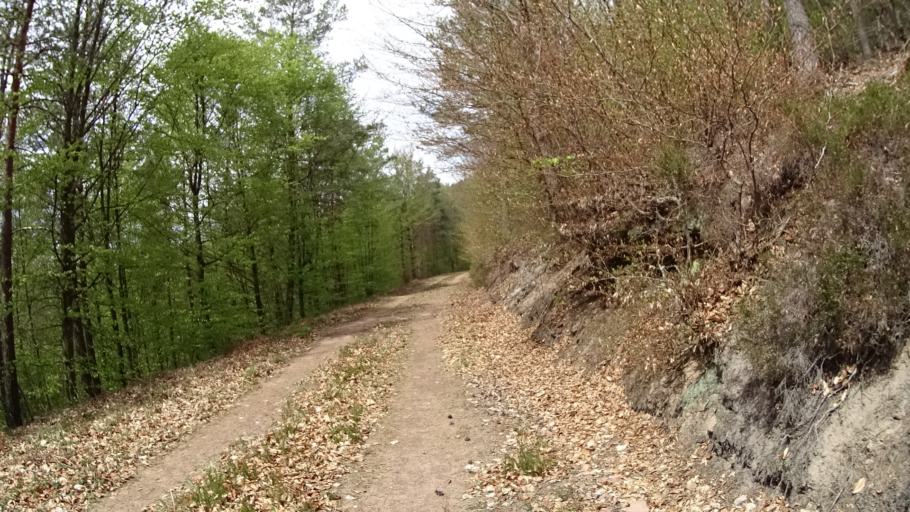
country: DE
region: Rheinland-Pfalz
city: Esthal
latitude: 49.3295
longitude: 8.0000
